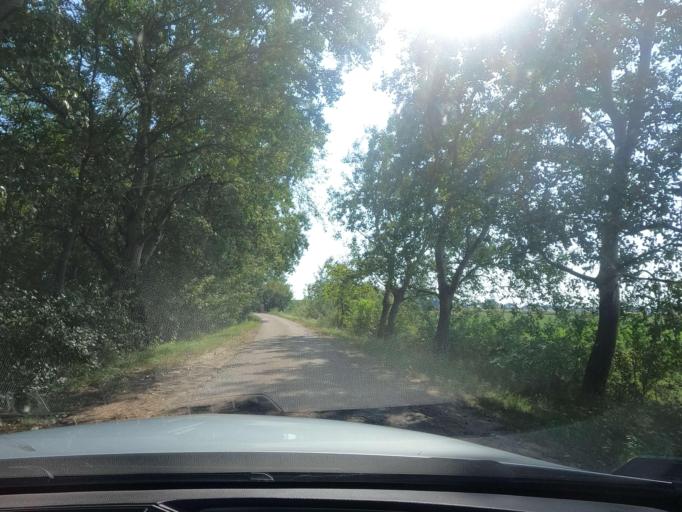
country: RS
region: Autonomna Pokrajina Vojvodina
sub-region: Juznobacki Okrug
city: Becej
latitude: 45.6581
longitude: 19.9020
